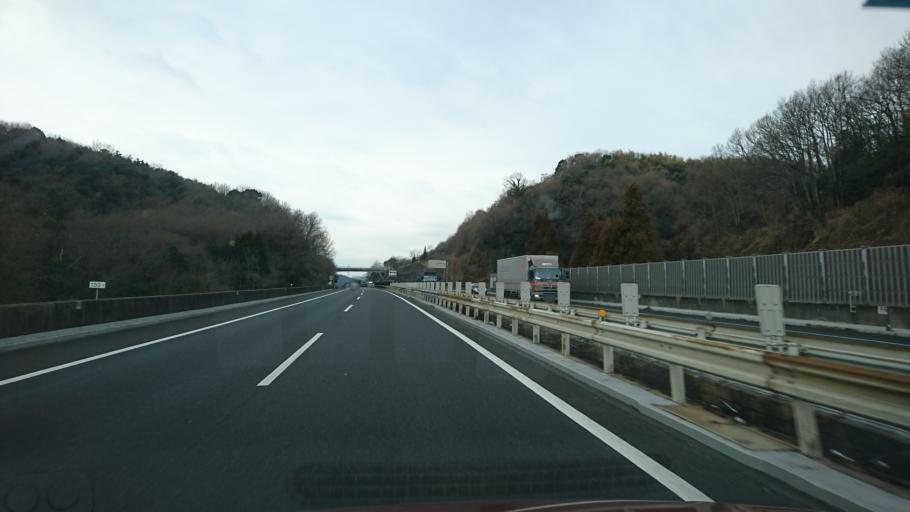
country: JP
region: Okayama
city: Kurashiki
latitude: 34.6257
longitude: 133.7636
